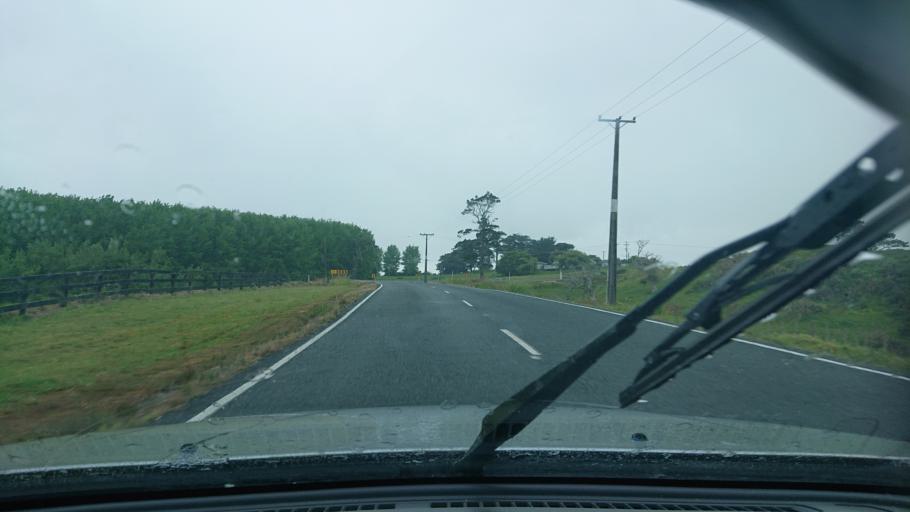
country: NZ
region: Auckland
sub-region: Auckland
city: Wellsford
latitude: -36.3280
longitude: 174.4072
